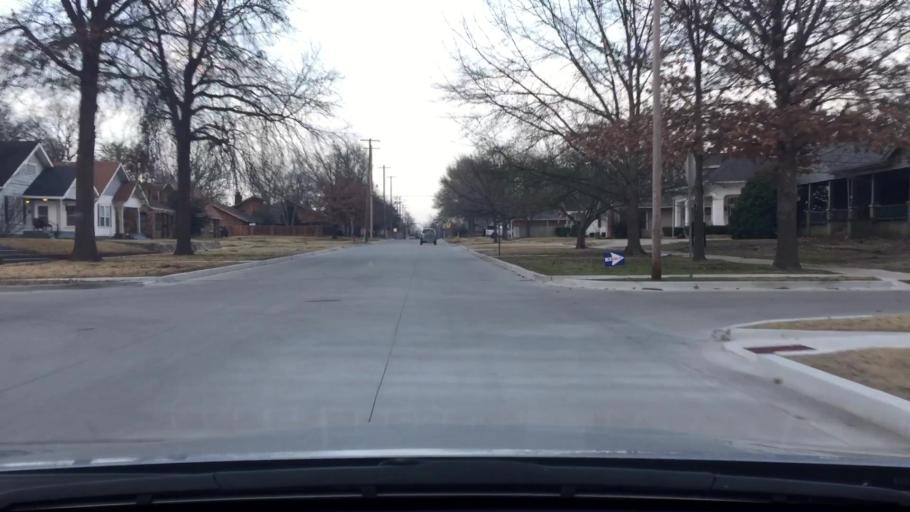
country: US
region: Oklahoma
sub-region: Carter County
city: Ardmore
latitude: 34.1710
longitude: -97.1398
